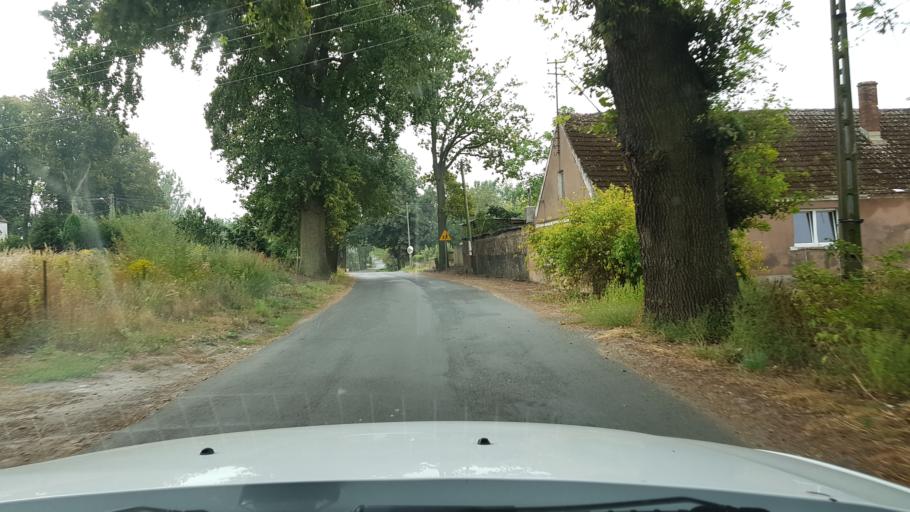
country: PL
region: West Pomeranian Voivodeship
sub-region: Powiat gryfinski
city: Moryn
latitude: 52.9004
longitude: 14.3752
